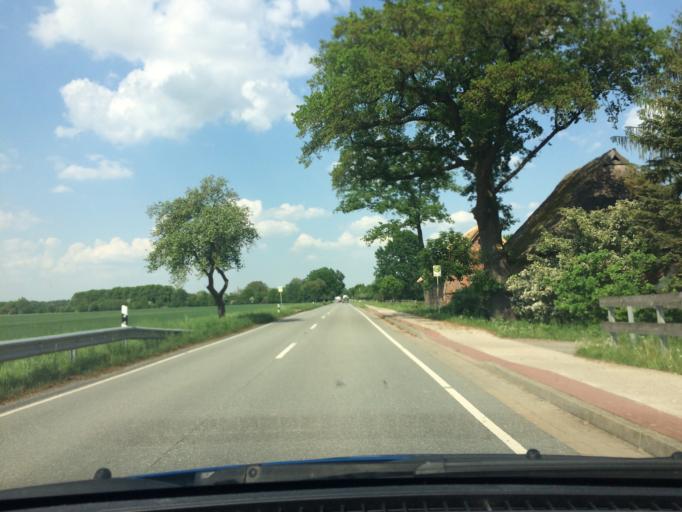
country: DE
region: Lower Saxony
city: Neu Darchau
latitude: 53.2734
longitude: 10.9256
